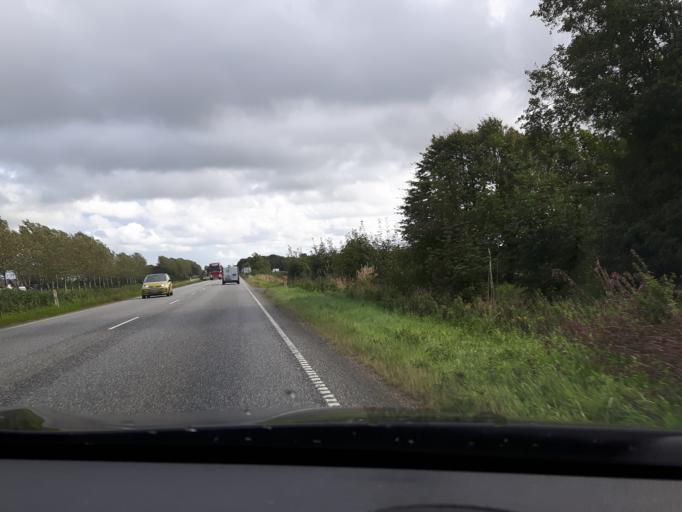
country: DK
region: Central Jutland
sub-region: Herning Kommune
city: Avlum
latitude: 56.2603
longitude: 8.7809
